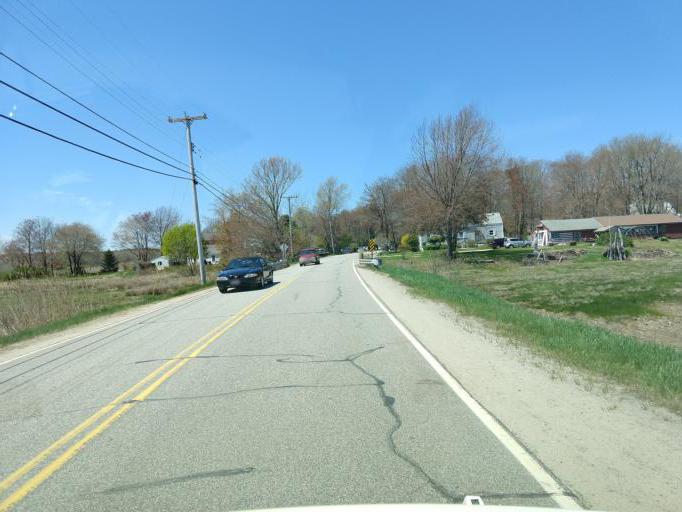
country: US
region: Maine
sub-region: York County
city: Old Orchard Beach
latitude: 43.4668
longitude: -70.3858
